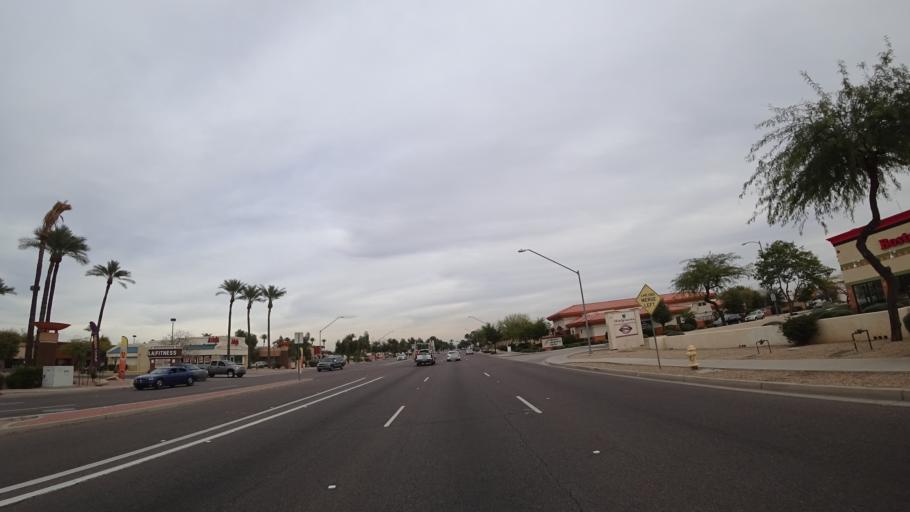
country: US
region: Arizona
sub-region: Maricopa County
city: Glendale
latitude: 33.5819
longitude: -112.1845
